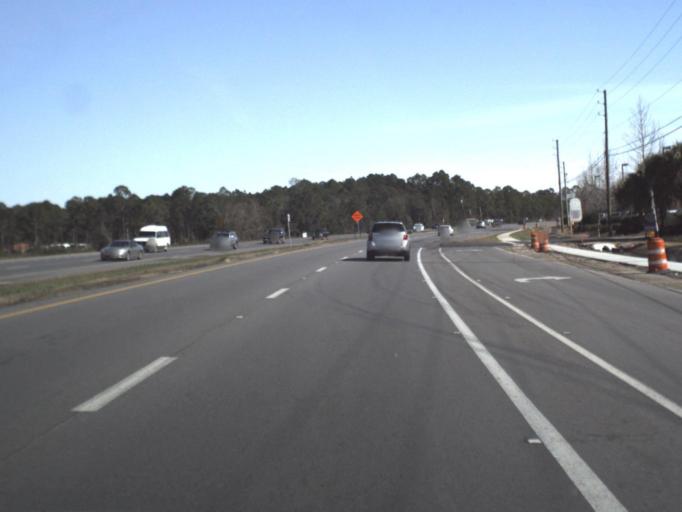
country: US
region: Florida
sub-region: Bay County
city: Panama City Beach
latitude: 30.2051
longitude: -85.8278
